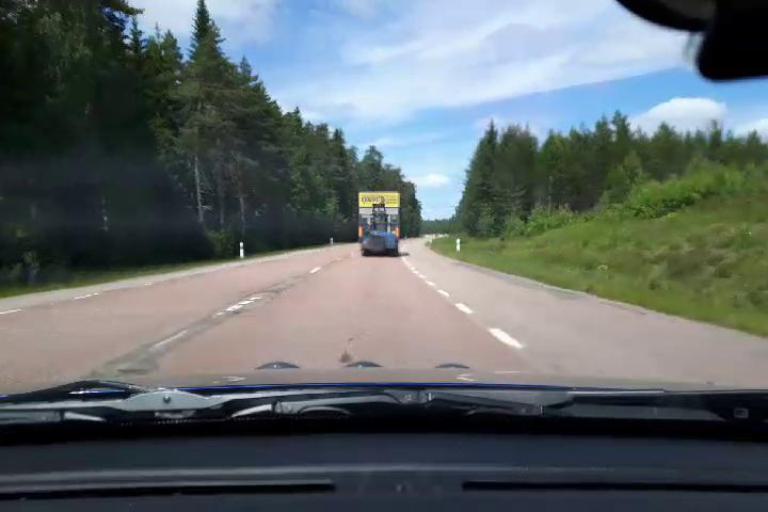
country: SE
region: Uppsala
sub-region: Osthammars Kommun
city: Bjorklinge
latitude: 60.1247
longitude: 17.5092
